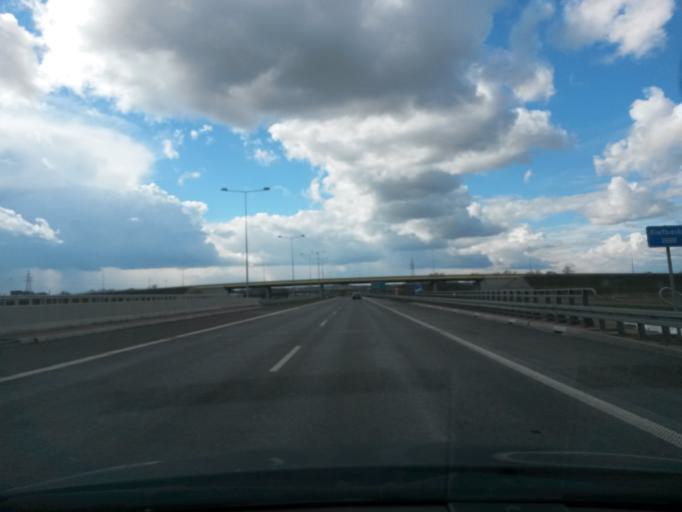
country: PL
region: Greater Poland Voivodeship
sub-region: Powiat turecki
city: Brudzew
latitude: 52.1394
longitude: 18.6164
